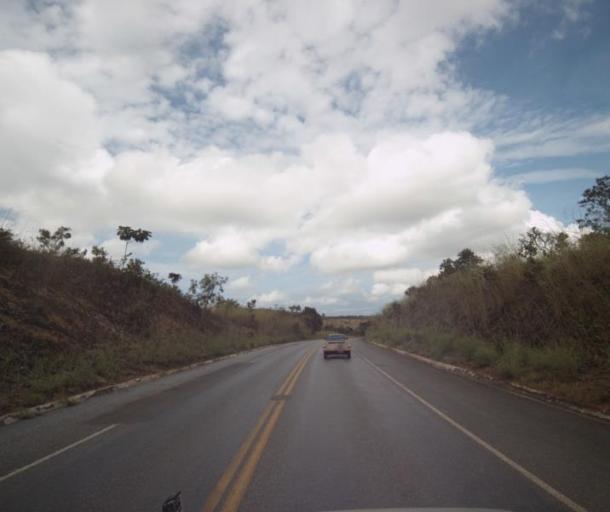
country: BR
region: Goias
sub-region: Pirenopolis
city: Pirenopolis
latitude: -15.6050
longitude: -48.6460
